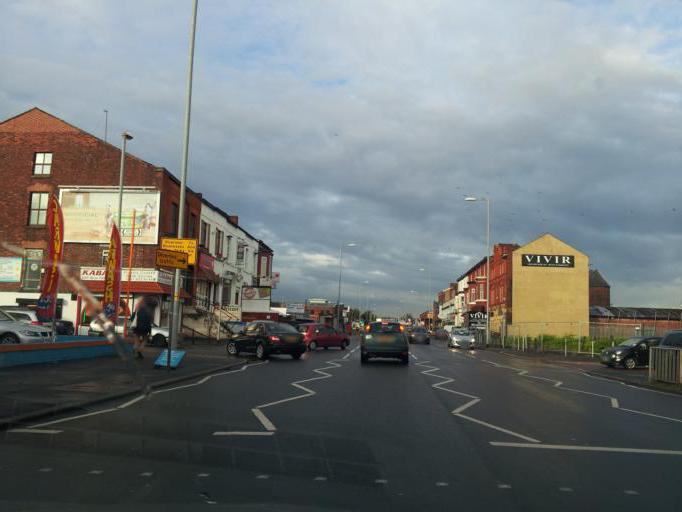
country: GB
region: England
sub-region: Manchester
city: Cheetham Hill
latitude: 53.4940
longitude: -2.2393
